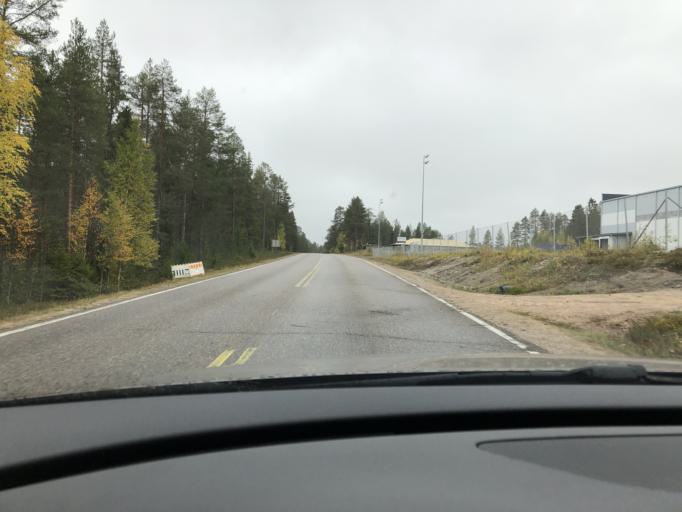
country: FI
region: Lapland
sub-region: Itae-Lappi
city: Posio
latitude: 66.1188
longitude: 28.1824
